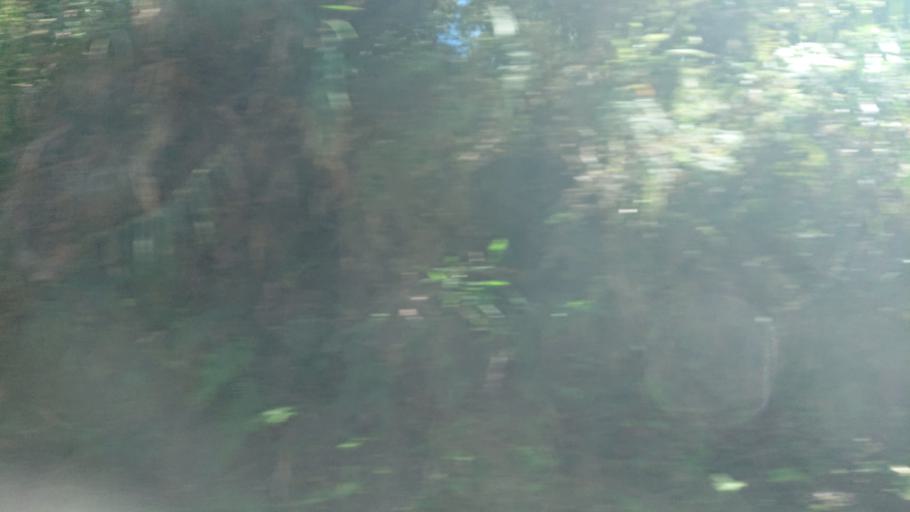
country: TW
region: Taiwan
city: Lugu
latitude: 23.4971
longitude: 120.7969
